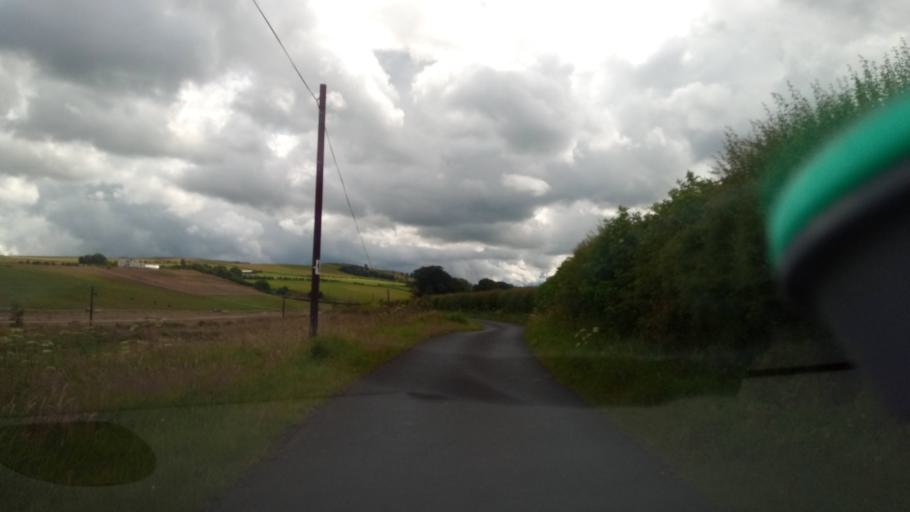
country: GB
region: Scotland
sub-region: The Scottish Borders
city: Kelso
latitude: 55.4942
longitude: -2.4280
